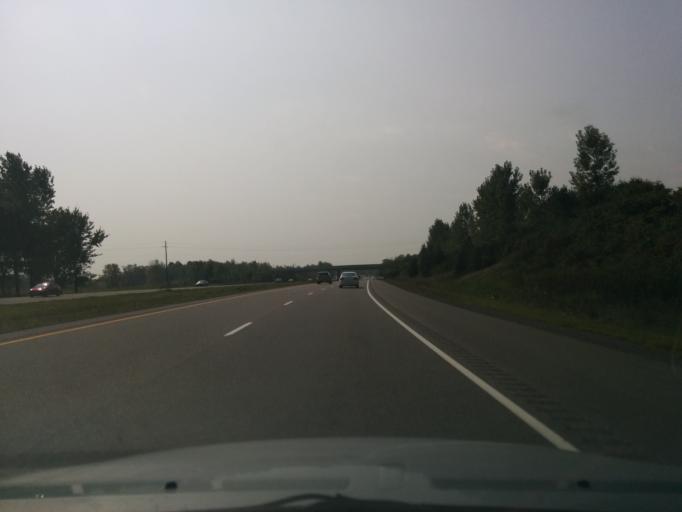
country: CA
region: Ontario
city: Bells Corners
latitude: 45.1290
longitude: -75.6750
